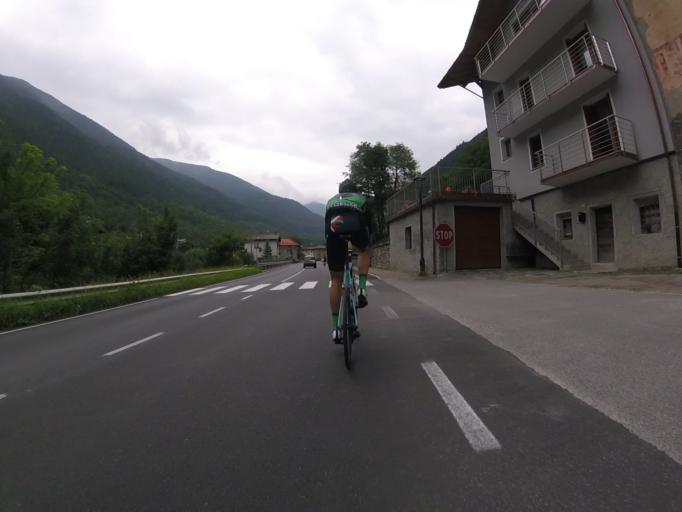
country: IT
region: Lombardy
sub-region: Provincia di Brescia
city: Incudine
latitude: 46.2192
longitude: 10.3572
